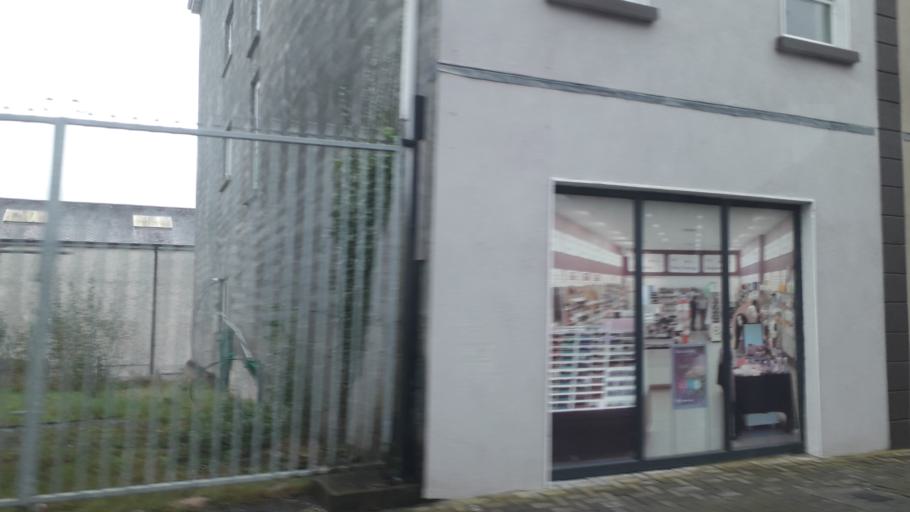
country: IE
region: Leinster
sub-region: An Longfort
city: Longford
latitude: 53.7305
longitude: -7.8022
